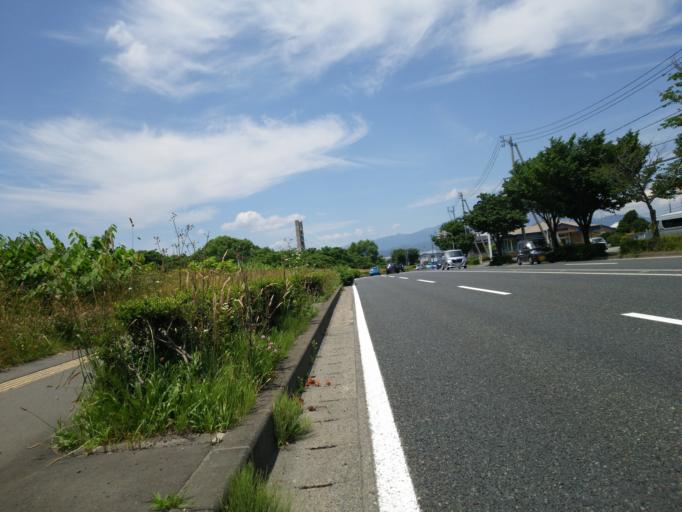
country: JP
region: Iwate
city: Morioka-shi
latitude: 39.7048
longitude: 141.1228
